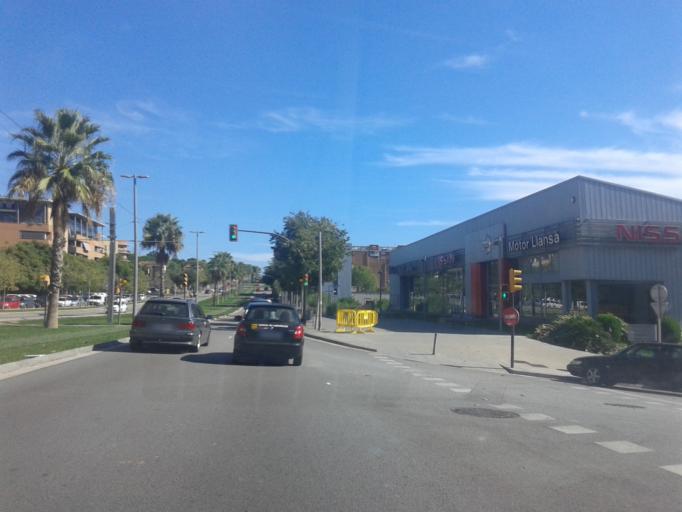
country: ES
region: Catalonia
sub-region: Provincia de Barcelona
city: Sant Just Desvern
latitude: 41.3795
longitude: 2.0679
